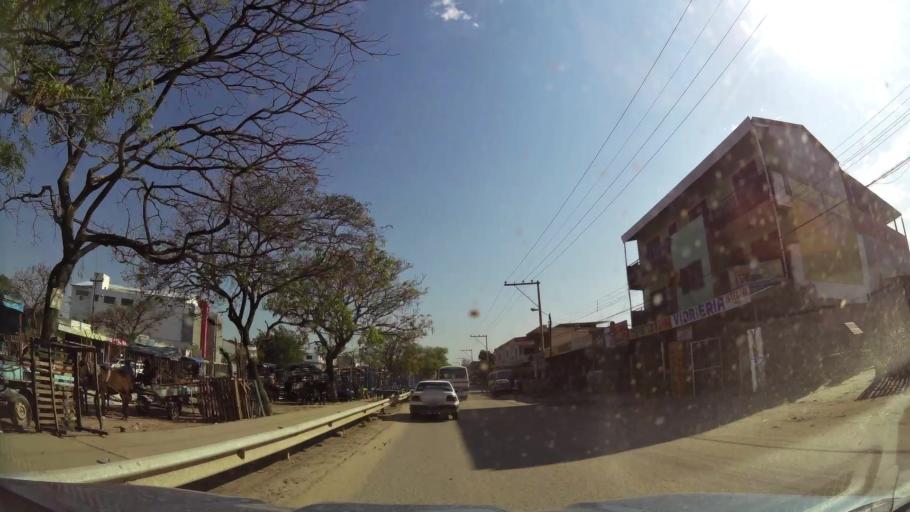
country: BO
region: Santa Cruz
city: Santa Cruz de la Sierra
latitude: -17.8270
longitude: -63.1358
